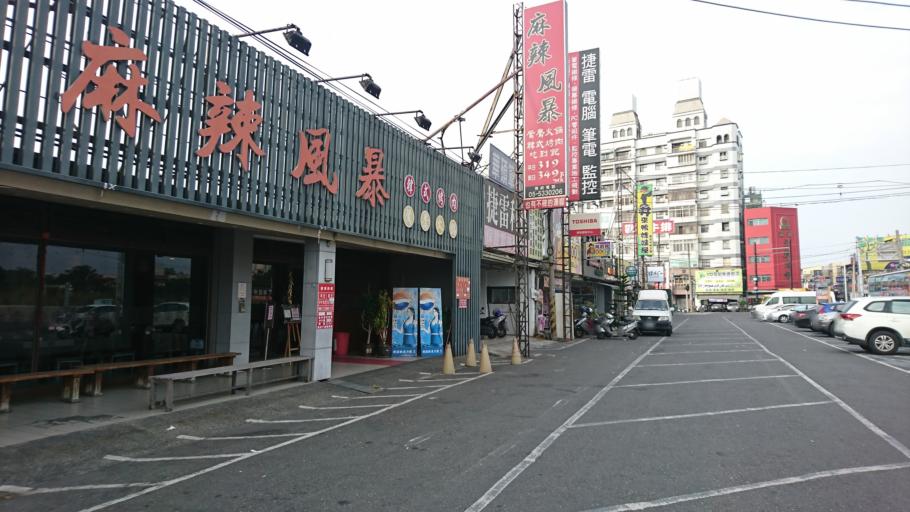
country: TW
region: Taiwan
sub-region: Yunlin
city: Douliu
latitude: 23.6972
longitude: 120.5379
